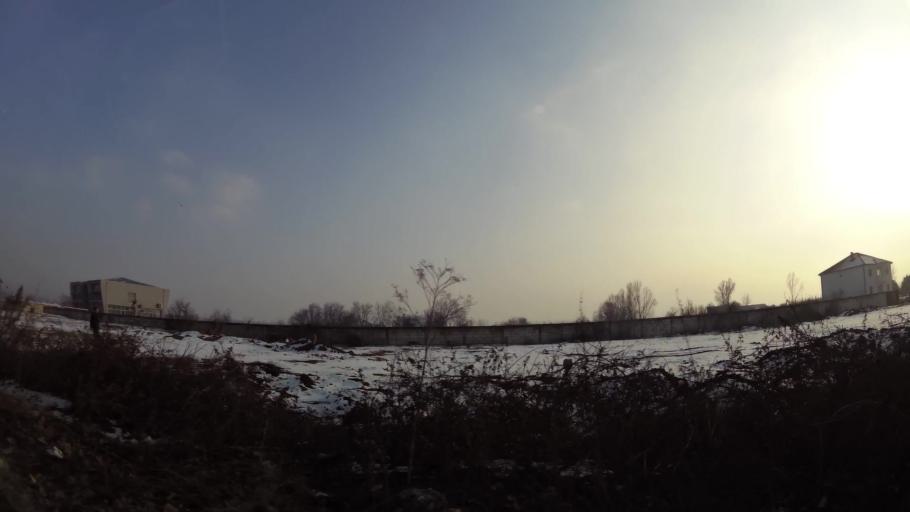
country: MK
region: Aracinovo
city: Arachinovo
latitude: 42.0229
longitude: 21.5494
